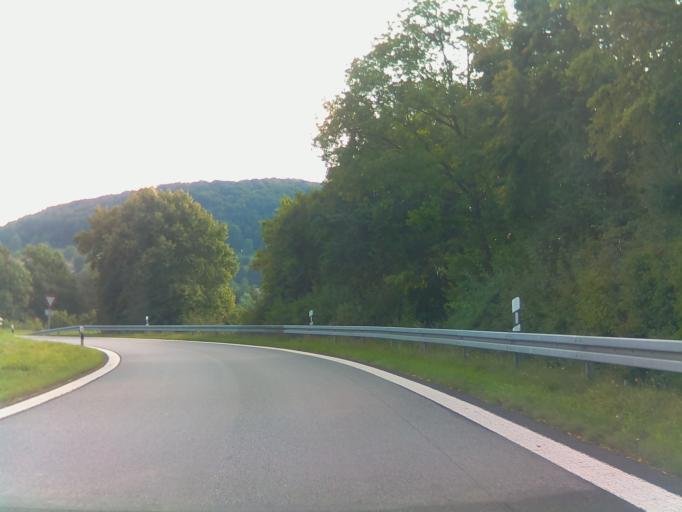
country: DE
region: Bavaria
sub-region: Regierungsbezirk Unterfranken
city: Elfershausen
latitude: 50.1257
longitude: 9.9573
